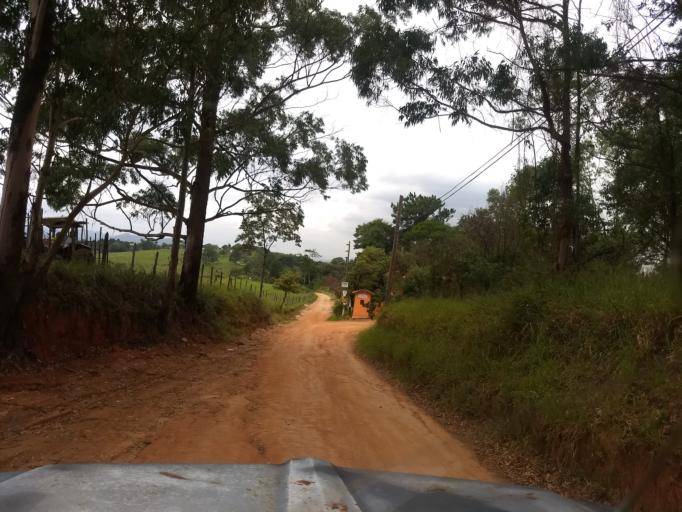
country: BR
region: Sao Paulo
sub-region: Cabreuva
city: Cabreuva
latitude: -23.3825
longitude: -47.1751
